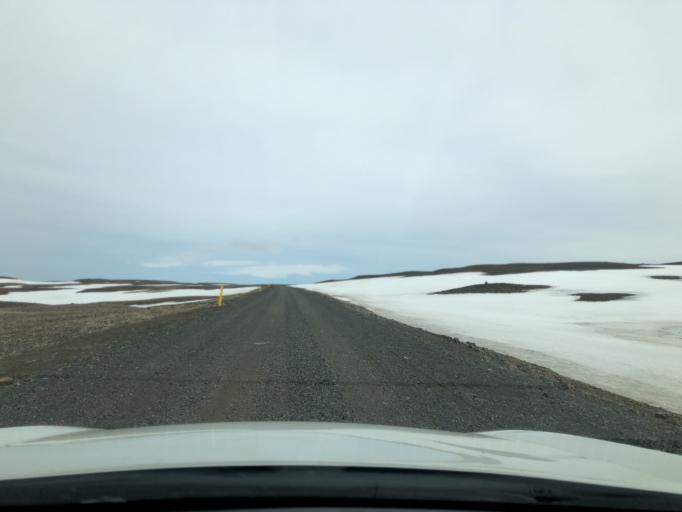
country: IS
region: East
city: Egilsstadir
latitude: 65.3041
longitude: -15.3979
